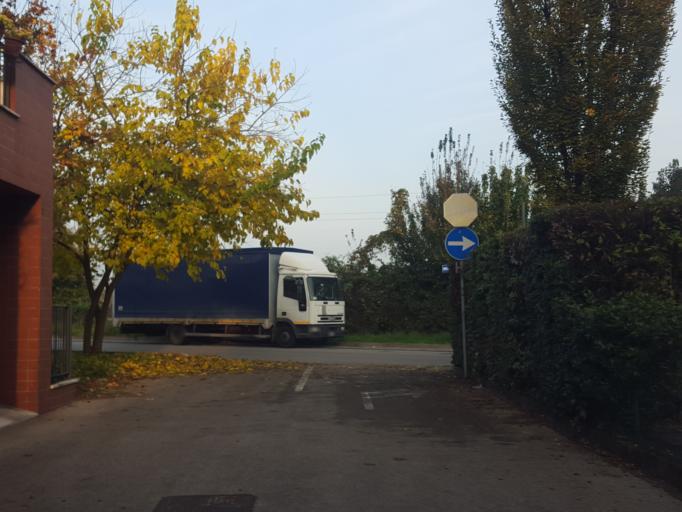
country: IT
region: Veneto
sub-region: Provincia di Vicenza
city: Vicenza
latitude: 45.5574
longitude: 11.5668
